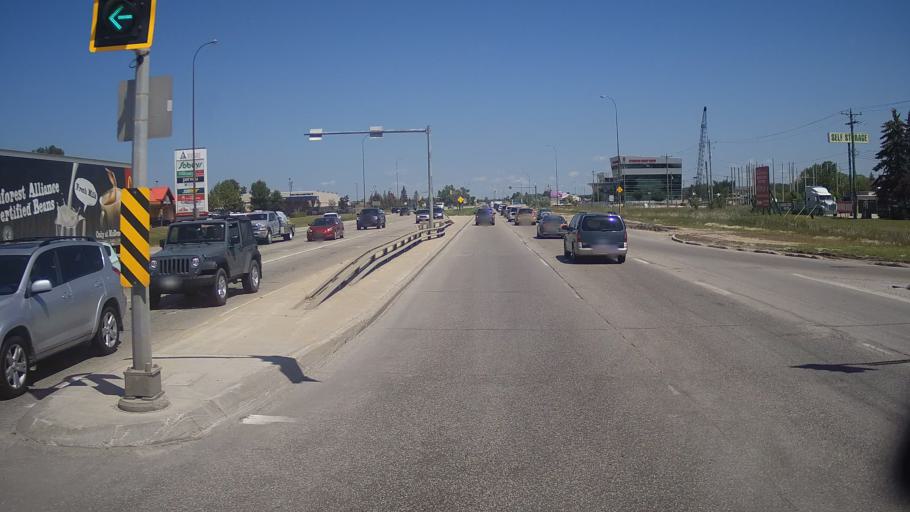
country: CA
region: Manitoba
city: Winnipeg
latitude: 49.9026
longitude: -97.0663
